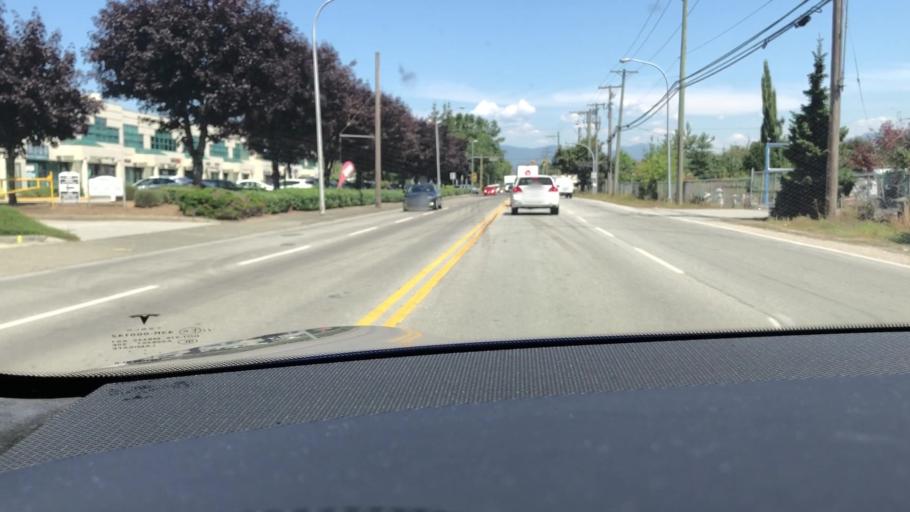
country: CA
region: British Columbia
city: Richmond
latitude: 49.1833
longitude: -123.0691
